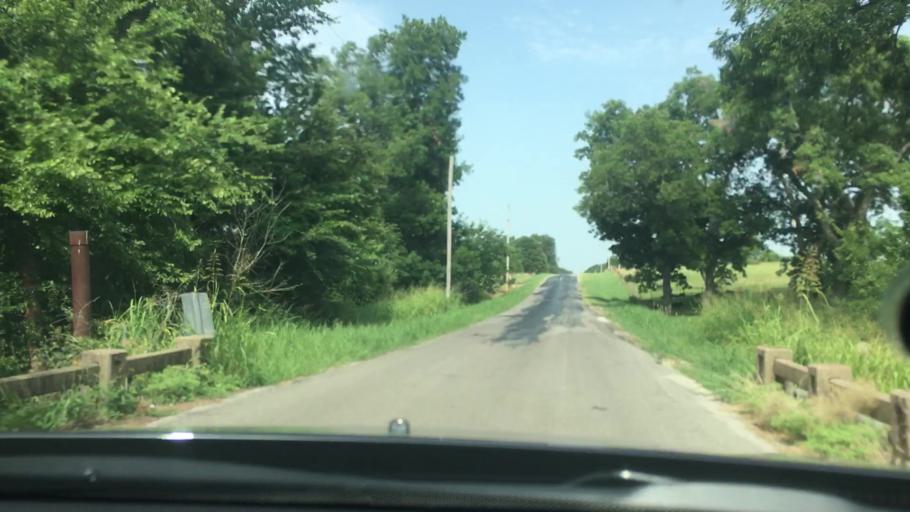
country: US
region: Oklahoma
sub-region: Garvin County
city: Pauls Valley
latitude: 34.8258
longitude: -97.2017
